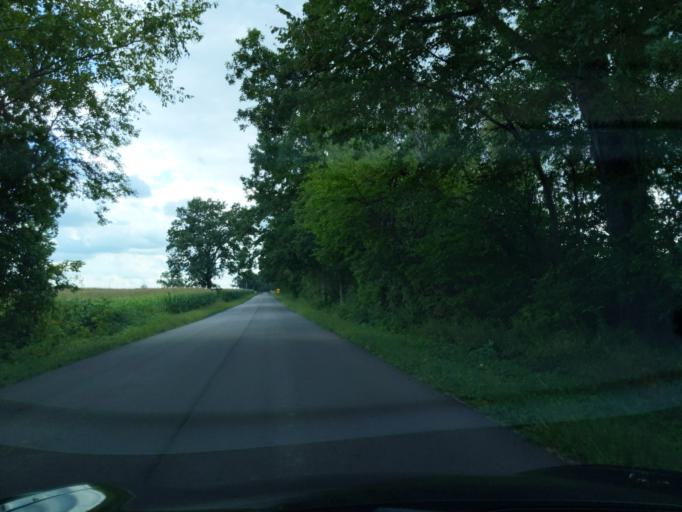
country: US
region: Michigan
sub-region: Eaton County
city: Eaton Rapids
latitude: 42.4544
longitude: -84.5804
